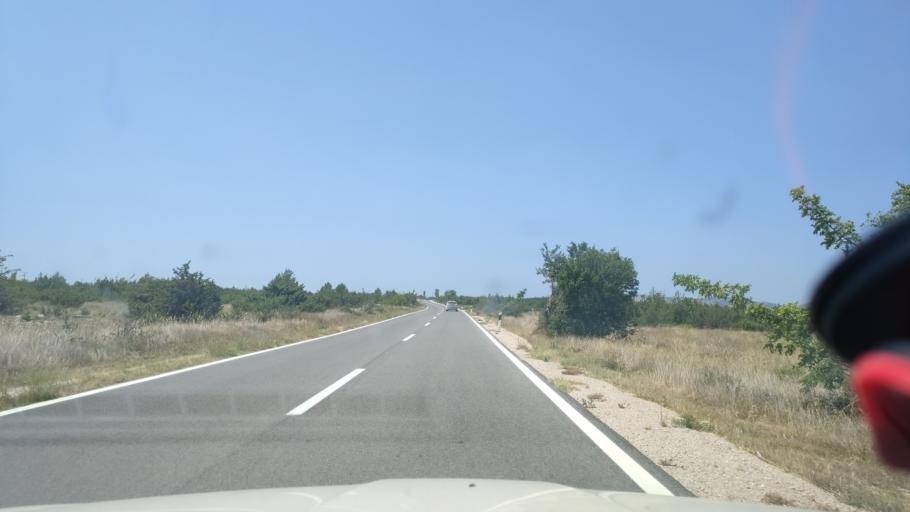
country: HR
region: Sibensko-Kniniska
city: Kistanje
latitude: 43.9676
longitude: 15.8763
